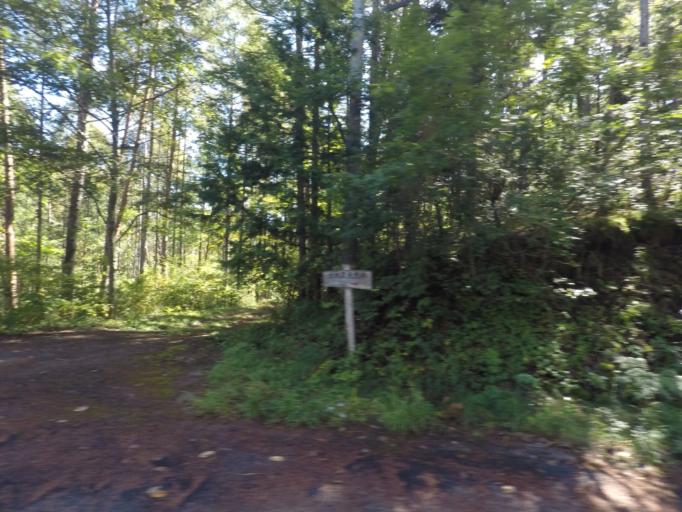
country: JP
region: Nagano
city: Shiojiri
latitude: 35.9932
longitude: 137.7352
